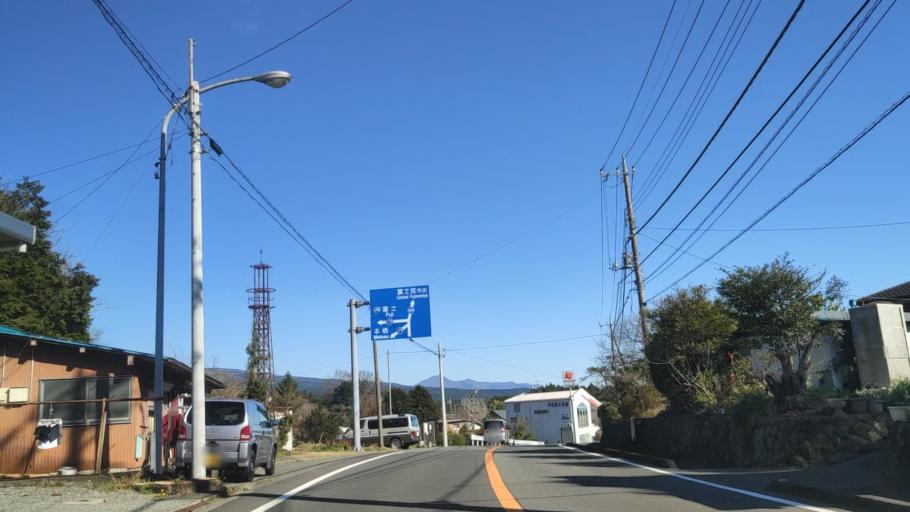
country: JP
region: Shizuoka
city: Fujinomiya
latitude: 35.3136
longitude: 138.5918
